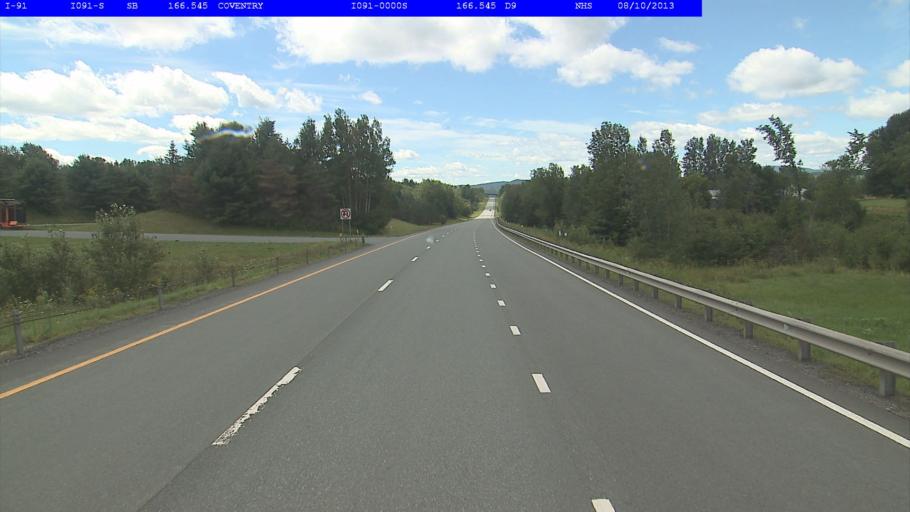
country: US
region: Vermont
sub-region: Orleans County
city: Newport
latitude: 44.8736
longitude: -72.1765
